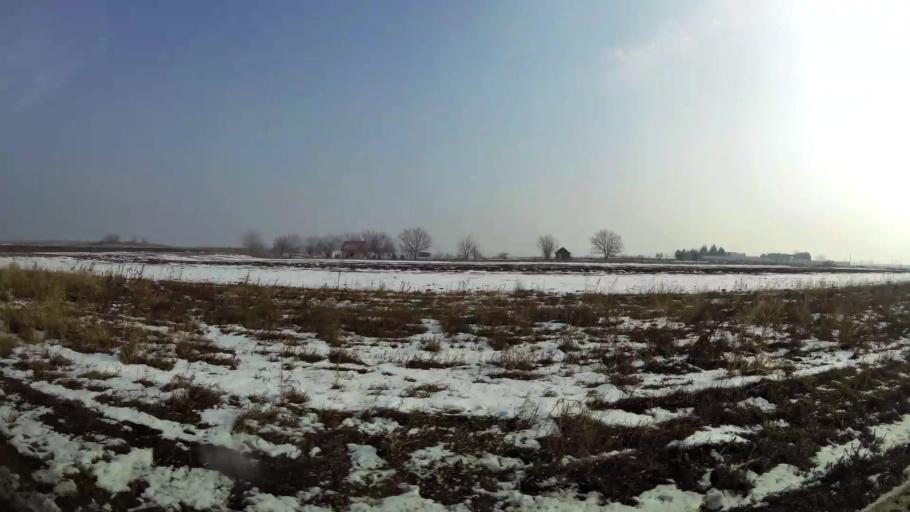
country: MK
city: Kadino
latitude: 41.9720
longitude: 21.6063
